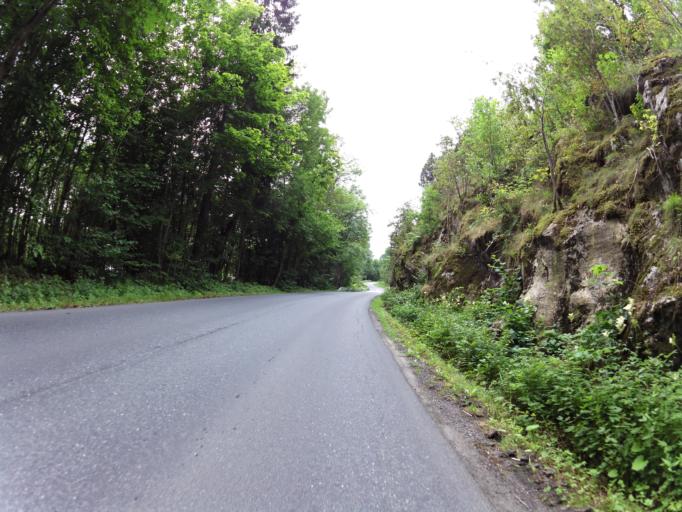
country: NO
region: Akershus
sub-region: As
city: As
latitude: 59.6970
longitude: 10.7385
